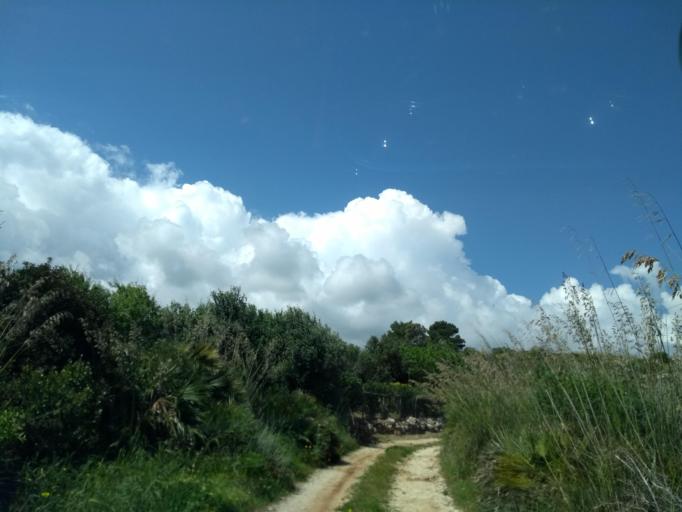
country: IT
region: Sicily
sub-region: Trapani
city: Castellammare del Golfo
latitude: 38.0510
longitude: 12.8517
